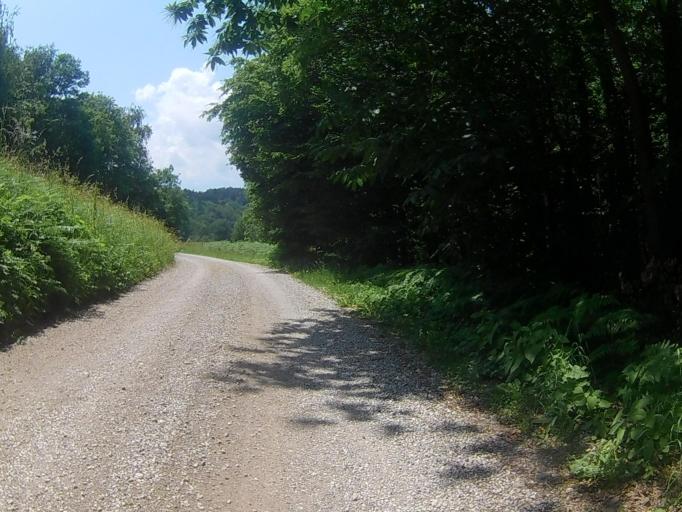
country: SI
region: Kungota
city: Zgornja Kungota
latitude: 46.6101
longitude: 15.5922
